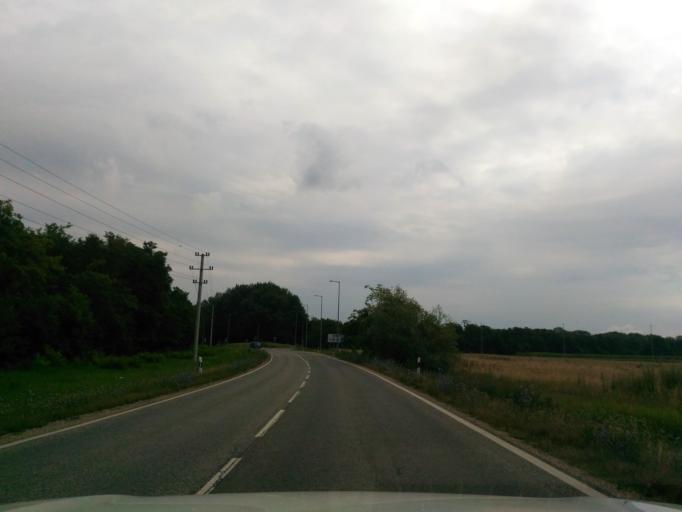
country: HU
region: Pest
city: Ujhartyan
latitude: 47.2122
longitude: 19.3921
